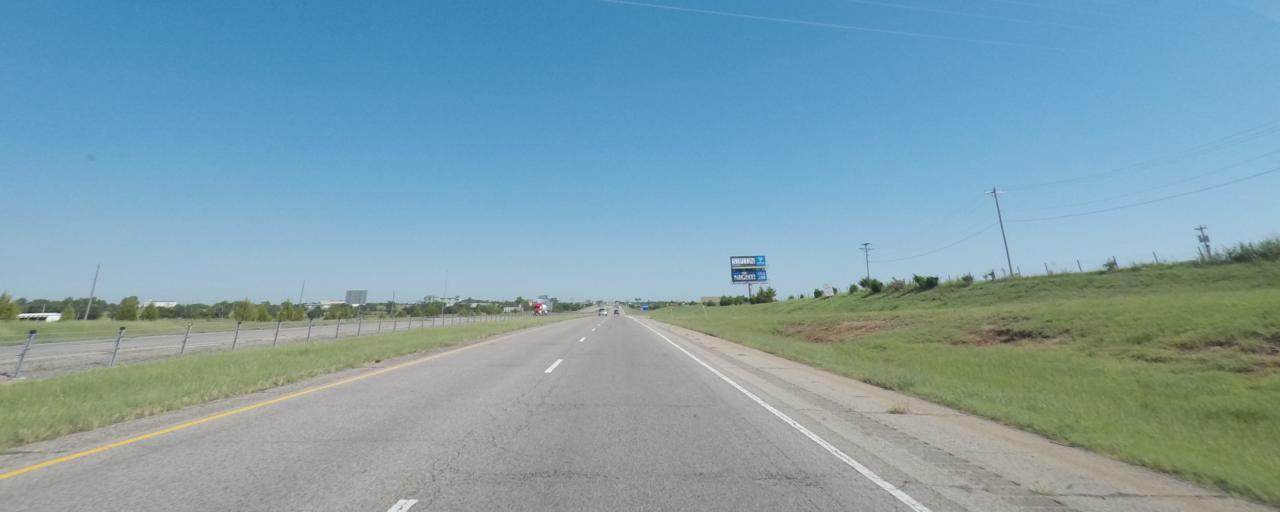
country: US
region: Oklahoma
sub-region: Noble County
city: Perry
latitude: 36.2769
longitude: -97.3276
